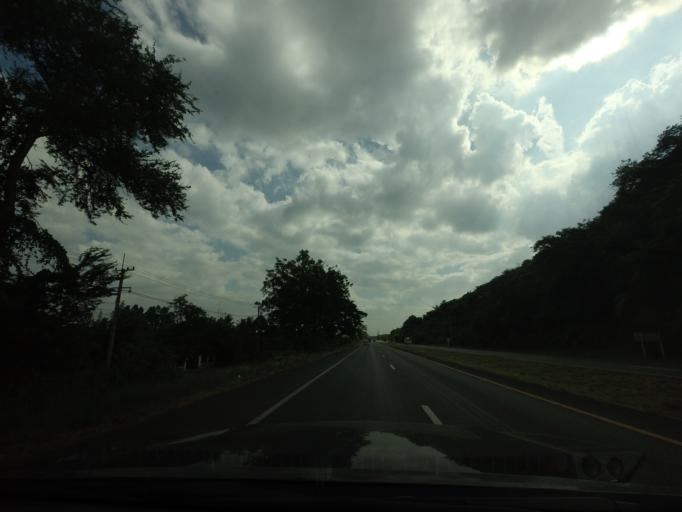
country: TH
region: Lop Buri
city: Chai Badan
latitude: 15.2952
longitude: 101.1290
